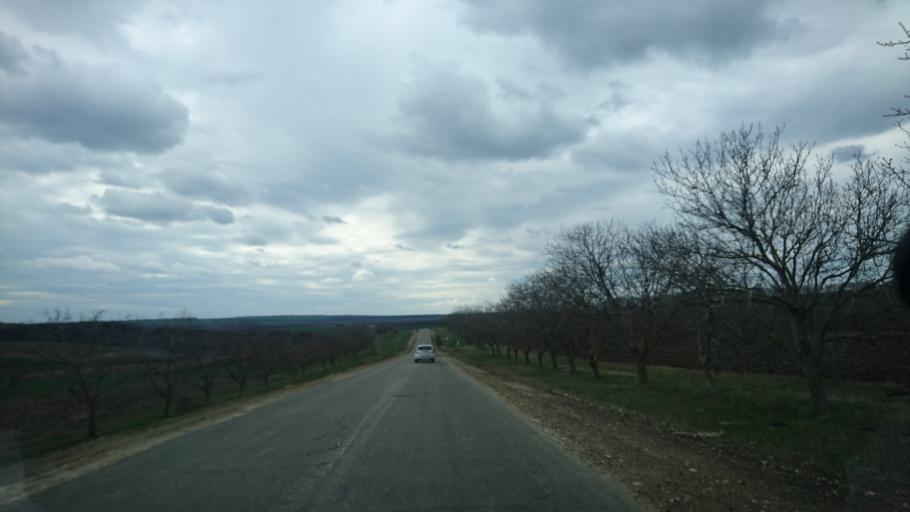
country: MD
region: Gagauzia
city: Comrat
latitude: 46.3095
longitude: 28.5981
